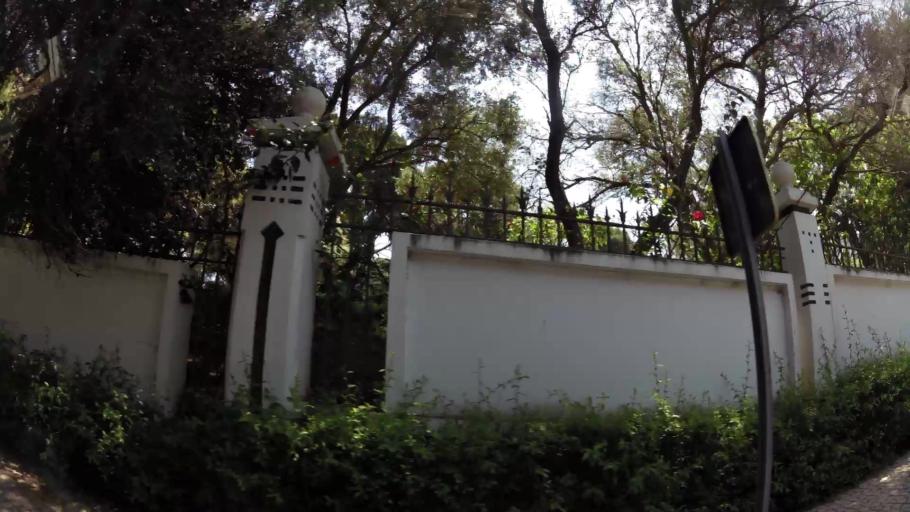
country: MA
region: Rabat-Sale-Zemmour-Zaer
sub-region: Rabat
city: Rabat
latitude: 34.0106
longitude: -6.8258
